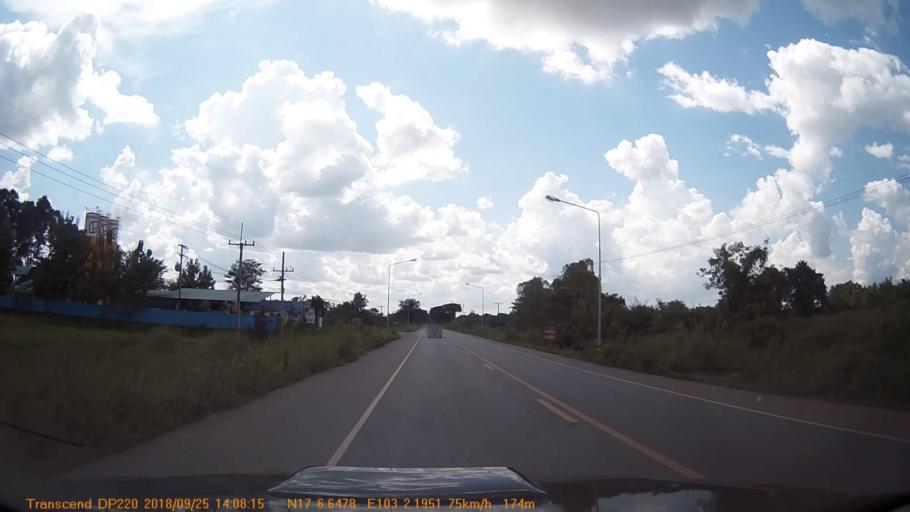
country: TH
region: Changwat Udon Thani
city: Kumphawapi
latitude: 17.1108
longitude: 103.0363
